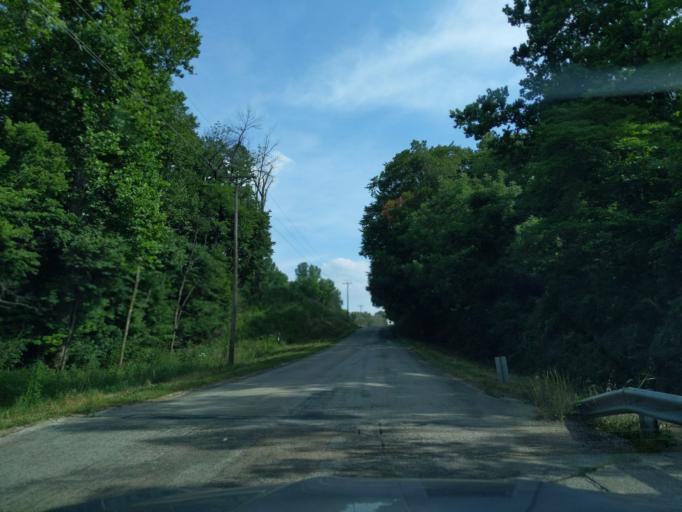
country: US
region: Indiana
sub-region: Decatur County
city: Greensburg
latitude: 39.2962
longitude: -85.4701
